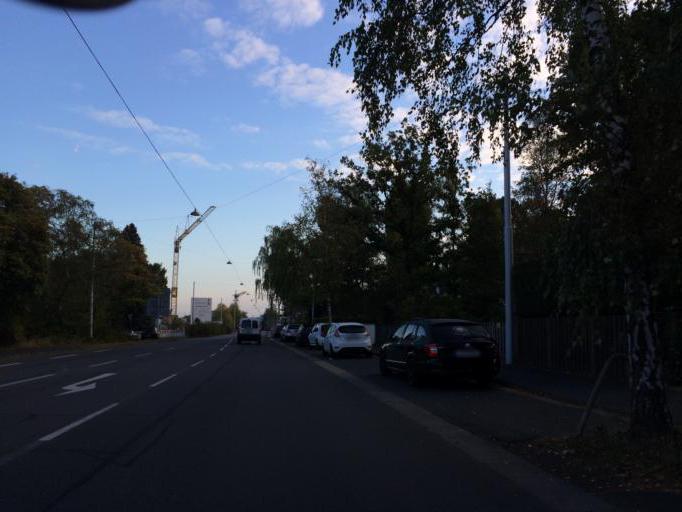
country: DE
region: North Rhine-Westphalia
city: Sankt Augustin
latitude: 50.7740
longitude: 7.1858
